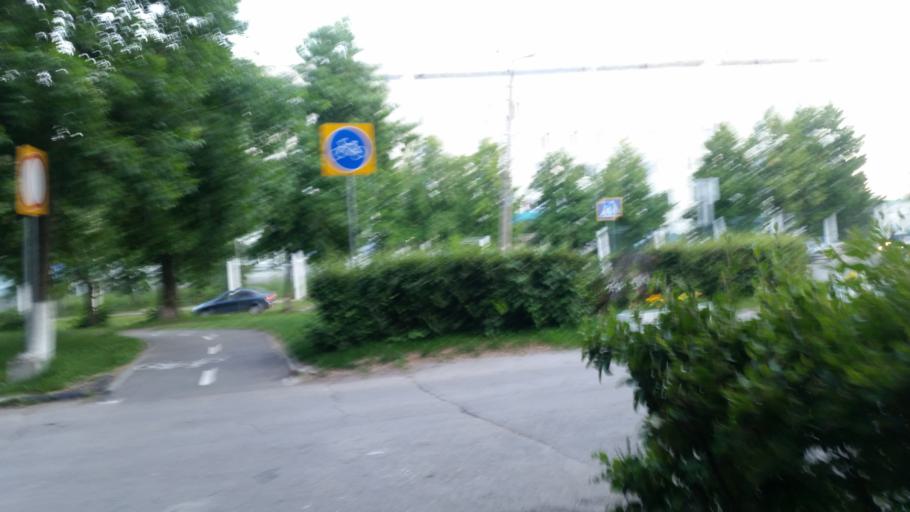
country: RU
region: Ulyanovsk
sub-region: Ulyanovskiy Rayon
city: Ulyanovsk
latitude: 54.3285
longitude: 48.4074
